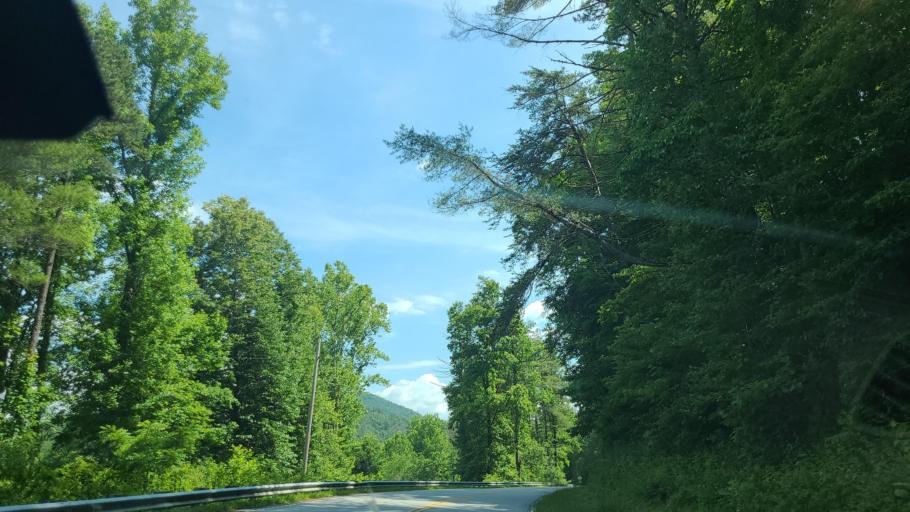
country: US
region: South Carolina
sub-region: Oconee County
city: Walhalla
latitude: 34.9141
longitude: -83.1691
